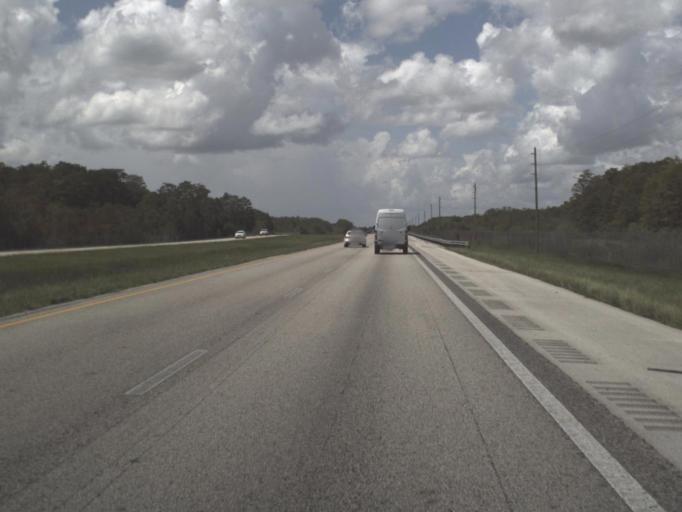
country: US
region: Florida
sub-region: Broward County
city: Weston
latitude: 26.1722
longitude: -80.9115
